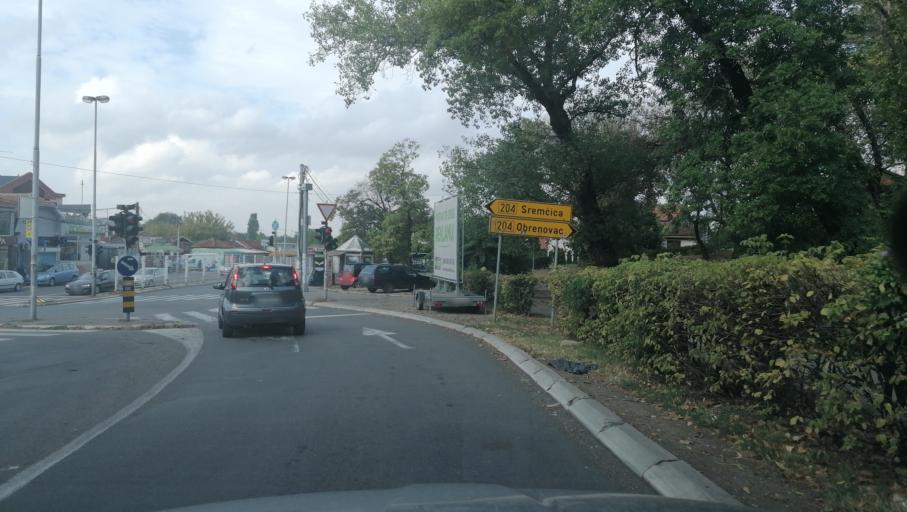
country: RS
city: Ostruznica
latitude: 44.7273
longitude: 20.3694
